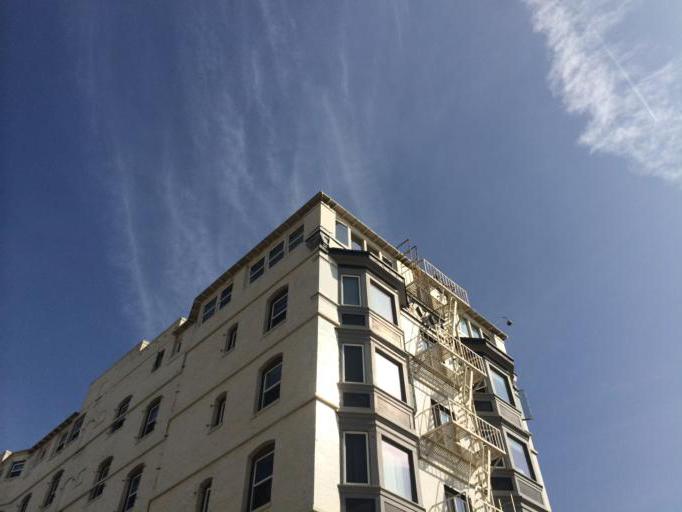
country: US
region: California
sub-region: Los Angeles County
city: Santa Monica
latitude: 33.9948
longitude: -118.4807
